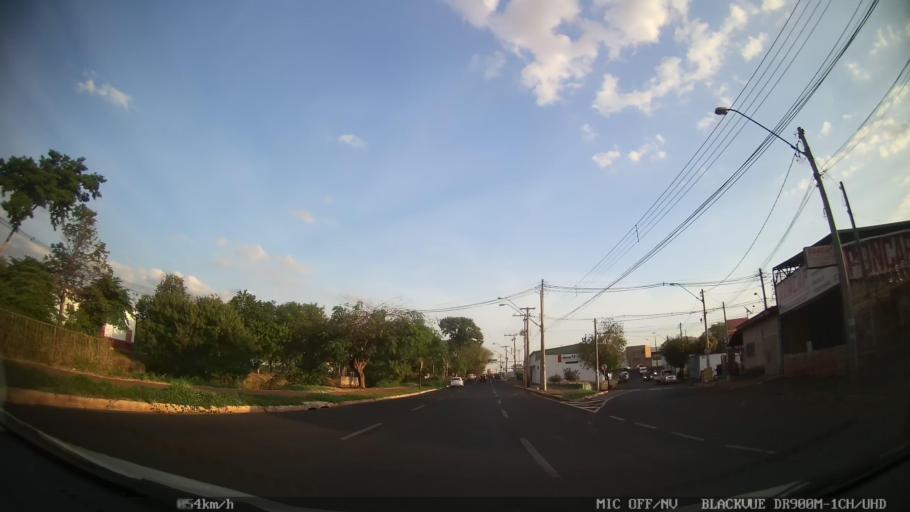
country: BR
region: Sao Paulo
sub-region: Ribeirao Preto
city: Ribeirao Preto
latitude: -21.1517
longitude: -47.8091
